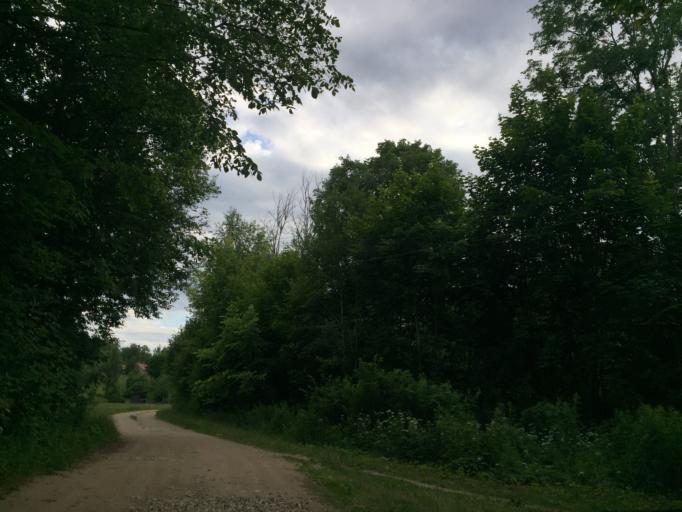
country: LV
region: Pargaujas
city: Stalbe
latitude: 57.3516
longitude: 24.9502
